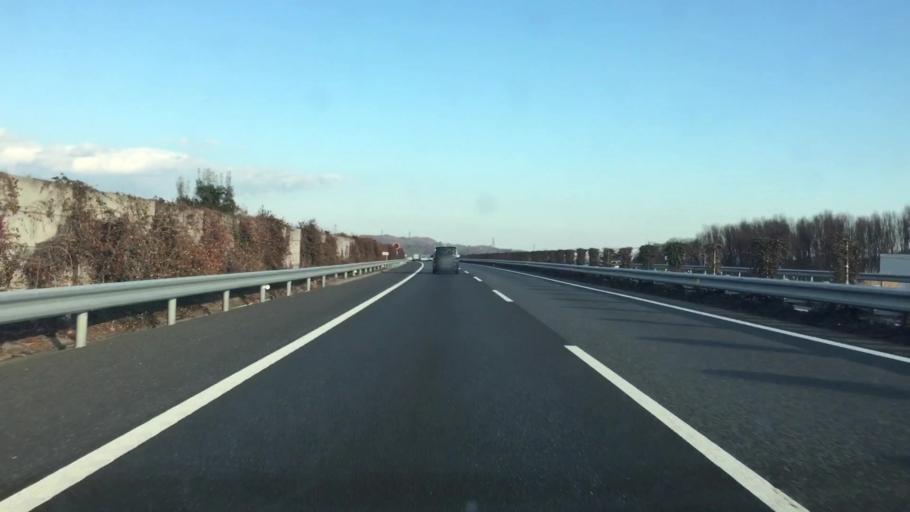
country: JP
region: Gunma
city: Kiryu
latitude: 36.3456
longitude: 139.2957
